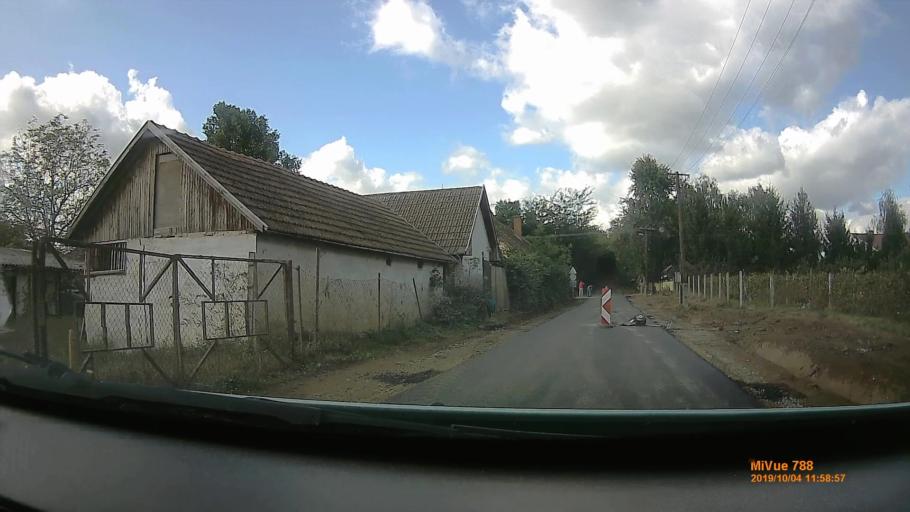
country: HU
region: Szabolcs-Szatmar-Bereg
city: Nyirtelek
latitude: 48.0168
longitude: 21.6697
